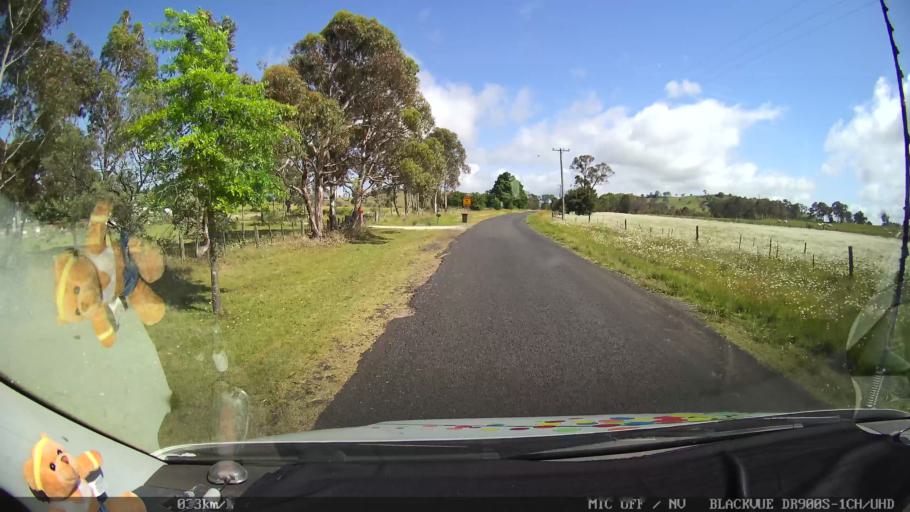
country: AU
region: New South Wales
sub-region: Guyra
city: Guyra
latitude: -30.0171
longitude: 151.6579
